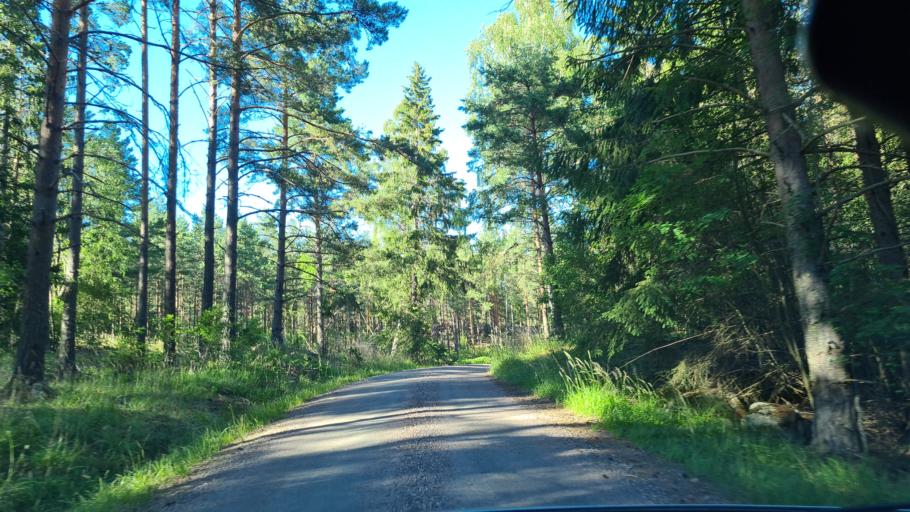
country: SE
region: Soedermanland
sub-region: Nykopings Kommun
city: Nykoping
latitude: 58.9109
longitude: 16.9427
